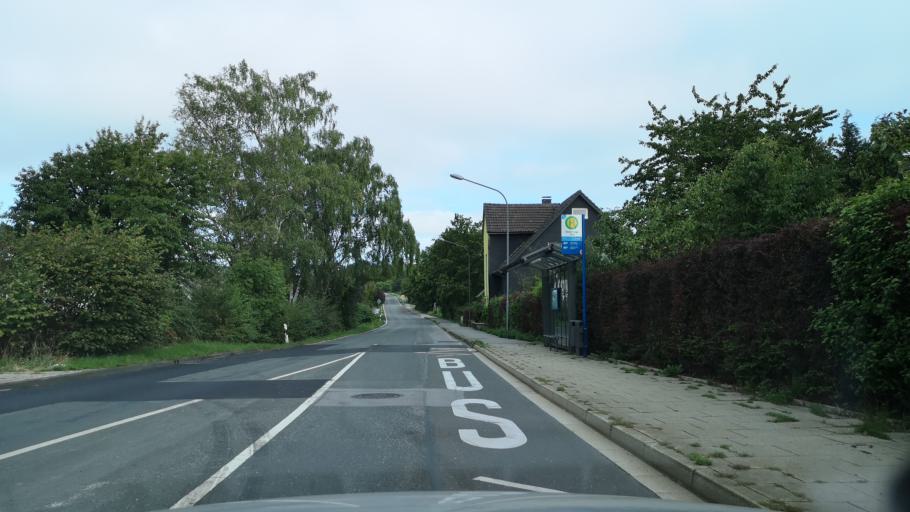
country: DE
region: North Rhine-Westphalia
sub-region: Regierungsbezirk Dusseldorf
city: Wuppertal
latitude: 51.3021
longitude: 7.1573
